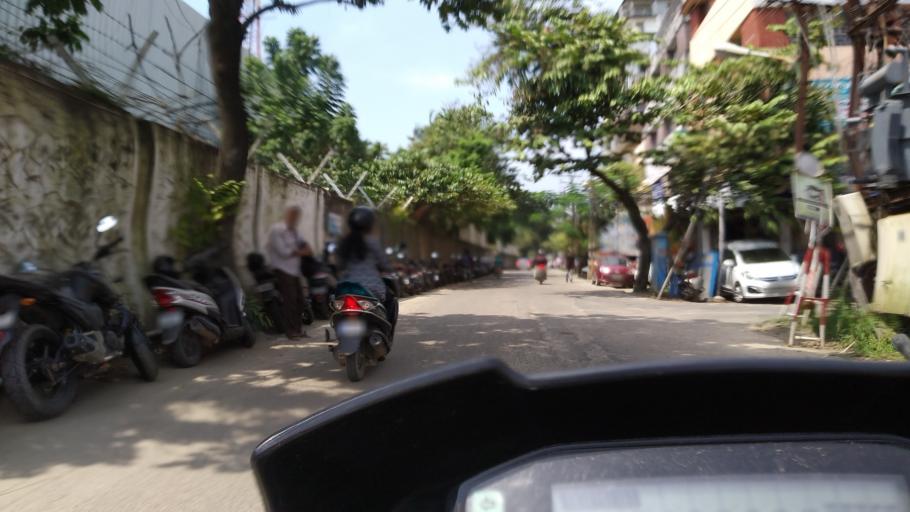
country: IN
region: Kerala
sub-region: Ernakulam
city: Cochin
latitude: 9.9607
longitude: 76.2870
